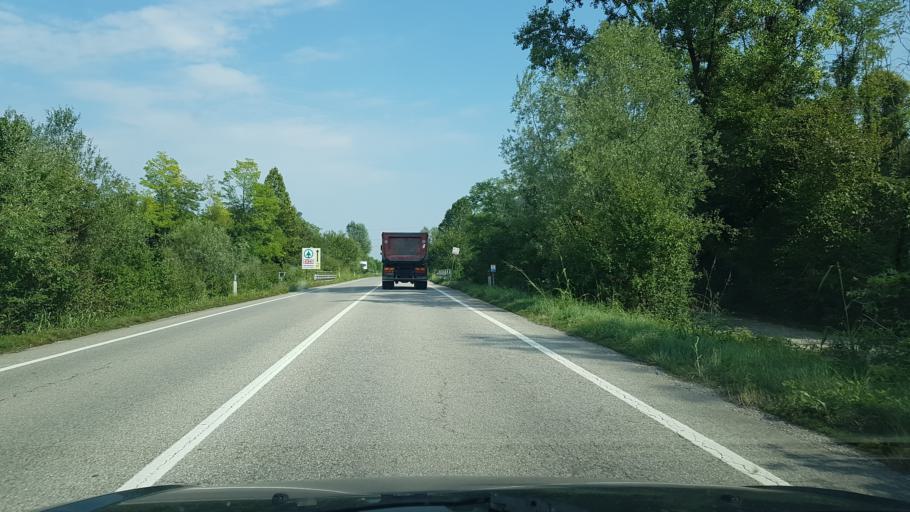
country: IT
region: Friuli Venezia Giulia
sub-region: Provincia di Pordenone
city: Spilimbergo
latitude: 46.0984
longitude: 12.8644
